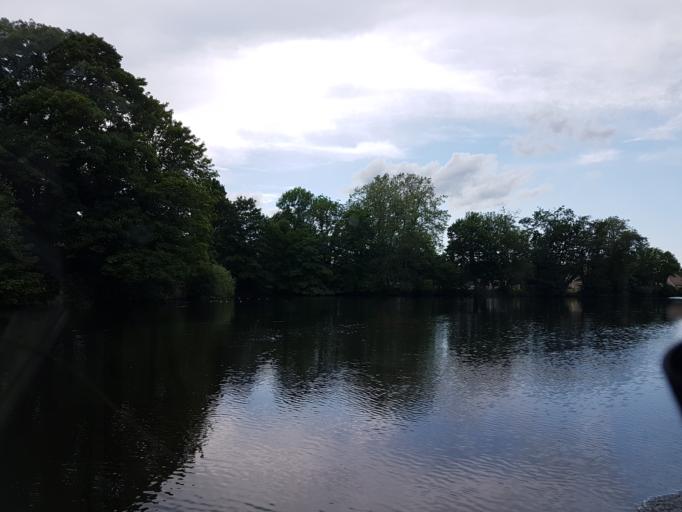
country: FR
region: Bourgogne
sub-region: Departement de l'Yonne
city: Moneteau
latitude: 47.8498
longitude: 3.5773
